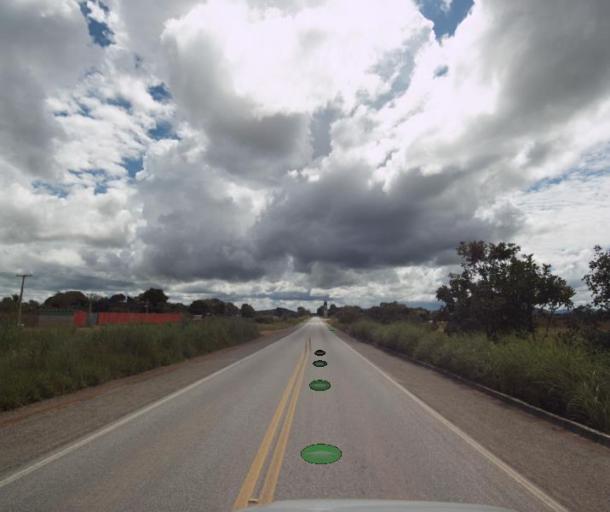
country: BR
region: Goias
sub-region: Uruacu
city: Uruacu
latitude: -14.2854
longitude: -49.1495
